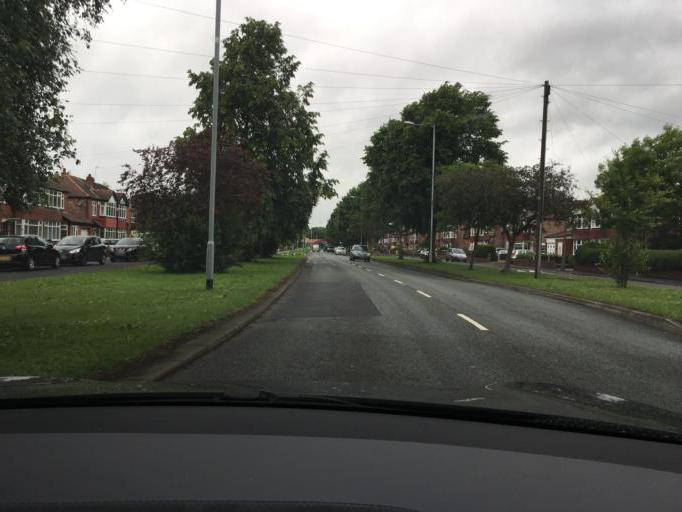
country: GB
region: England
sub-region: Borough of Stockport
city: Cheadle Heath
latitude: 53.3916
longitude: -2.1968
